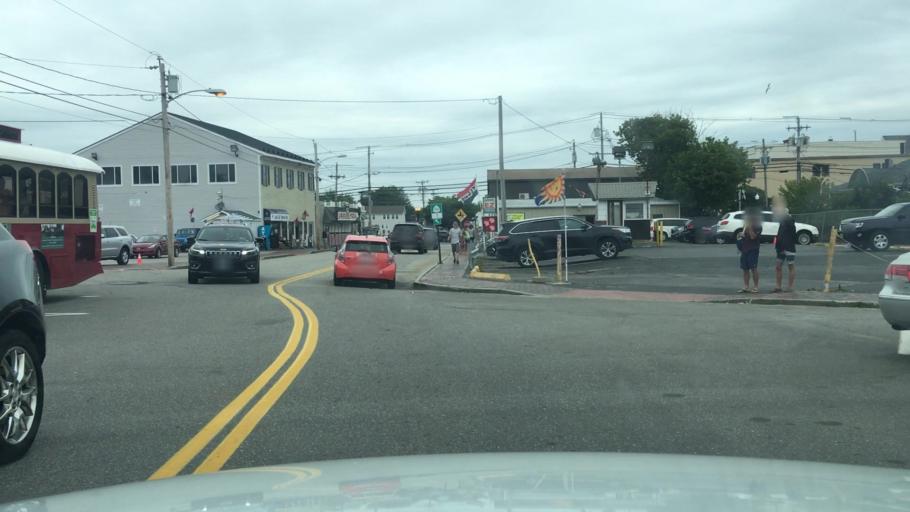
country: US
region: Maine
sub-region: York County
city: Old Orchard Beach
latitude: 43.5152
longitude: -70.3757
